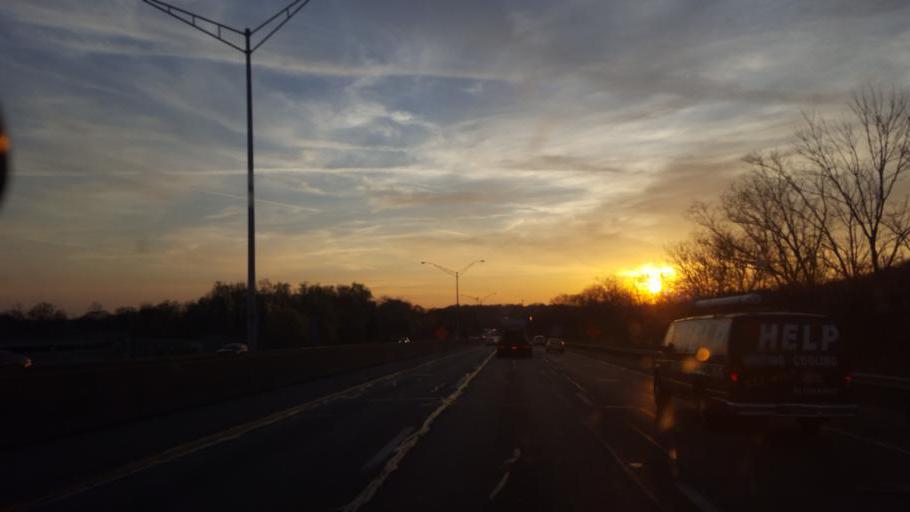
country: US
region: Ohio
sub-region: Hamilton County
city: Silverton
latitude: 39.1709
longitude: -84.4072
